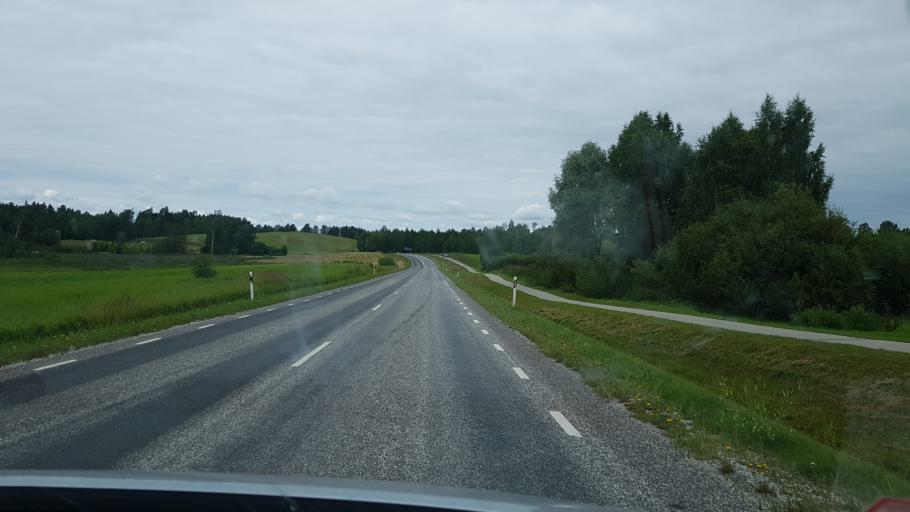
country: EE
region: Vorumaa
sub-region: Antsla vald
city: Vana-Antsla
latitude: 58.0538
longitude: 26.5357
